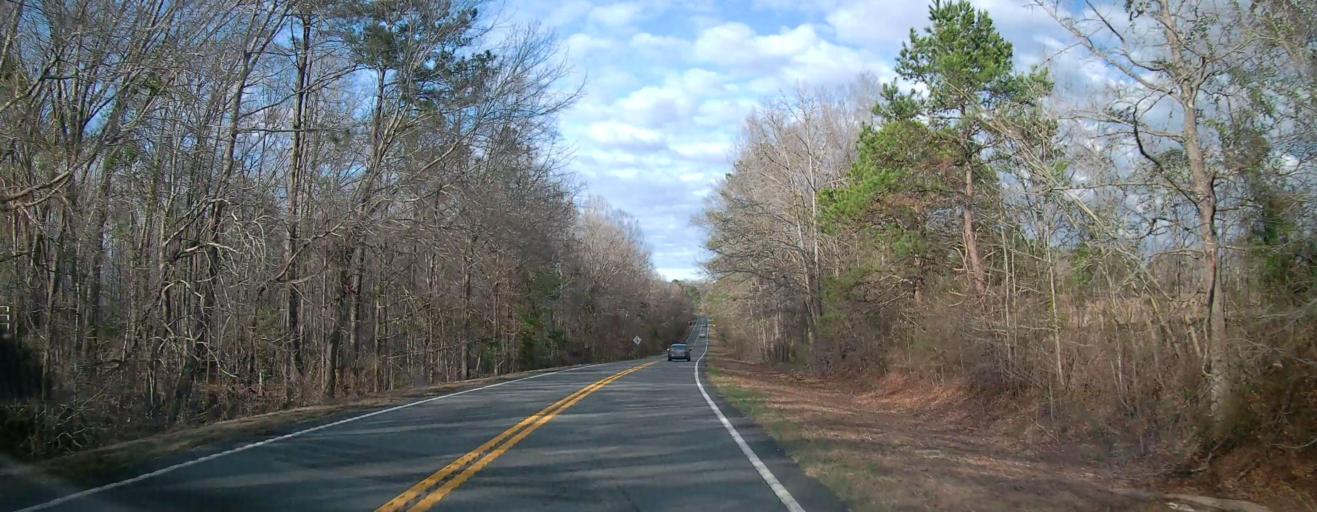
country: US
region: Georgia
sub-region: Talbot County
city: Talbotton
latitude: 32.5388
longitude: -84.6031
